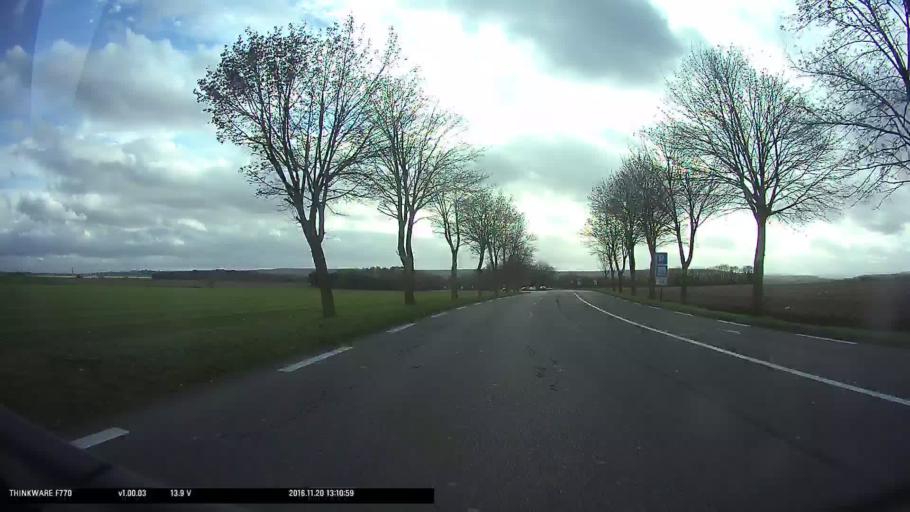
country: FR
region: Ile-de-France
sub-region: Departement du Val-d'Oise
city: Sagy
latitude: 49.0639
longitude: 1.9619
